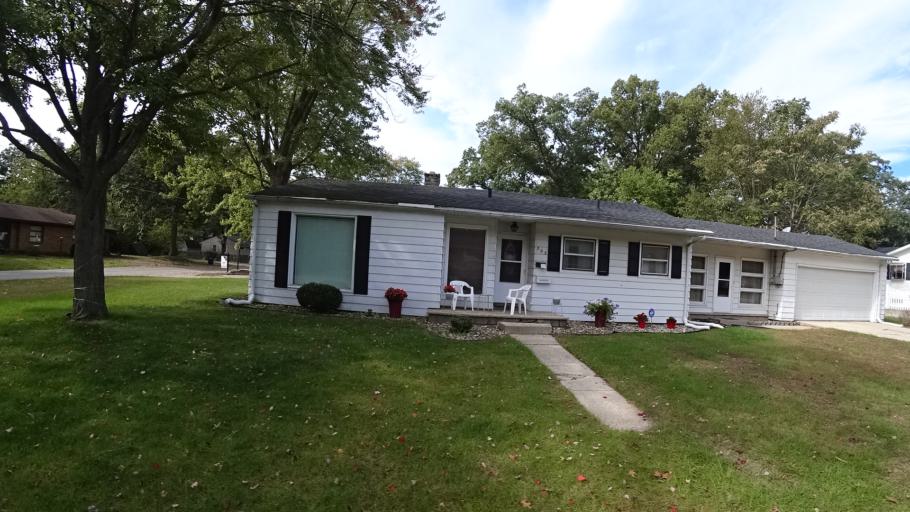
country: US
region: Indiana
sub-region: LaPorte County
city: Michigan City
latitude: 41.7155
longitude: -86.8776
